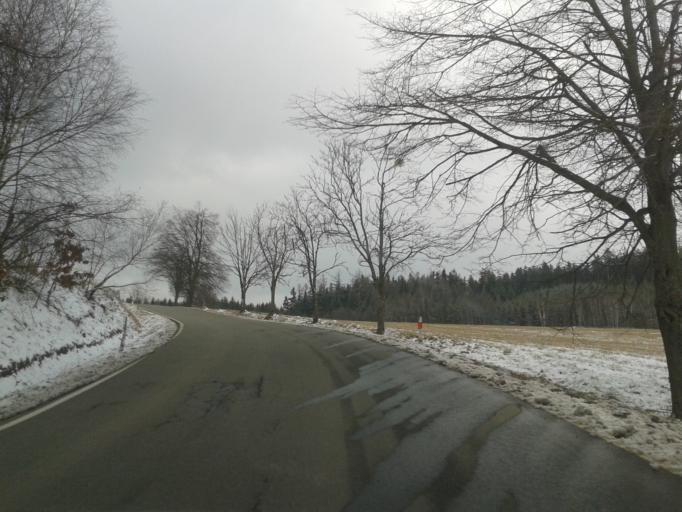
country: CZ
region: Olomoucky
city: Horni Stepanov
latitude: 49.5608
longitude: 16.8086
